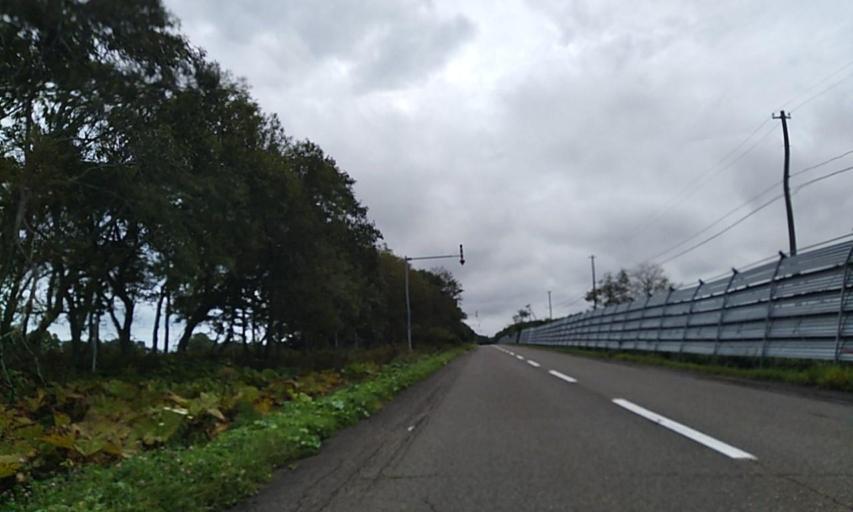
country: JP
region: Hokkaido
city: Nemuro
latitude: 43.3721
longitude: 145.2820
